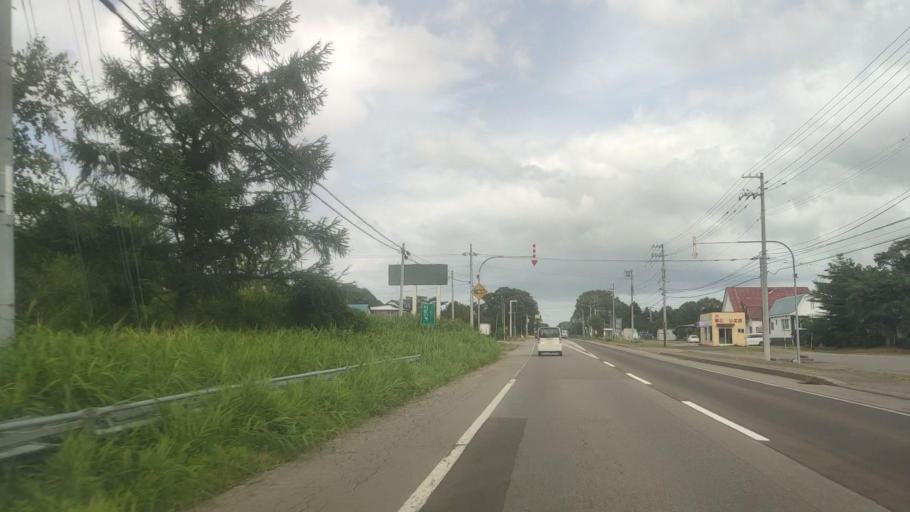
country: JP
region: Hokkaido
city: Nanae
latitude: 42.0349
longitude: 140.6079
